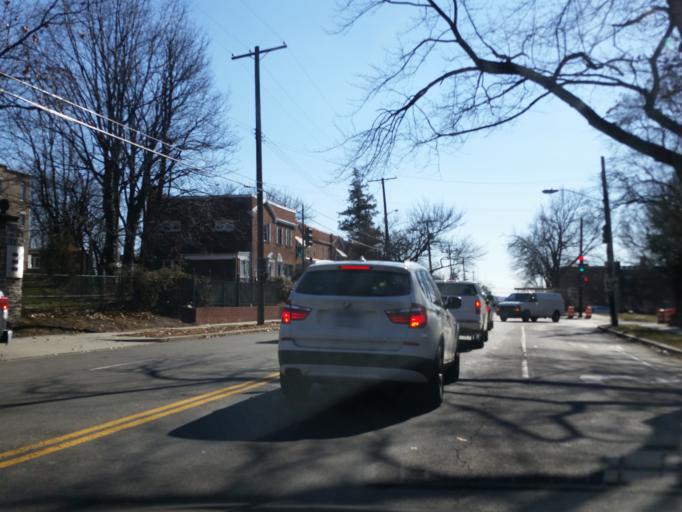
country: US
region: Maryland
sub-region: Prince George's County
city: Chillum
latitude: 38.9271
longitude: -77.0006
